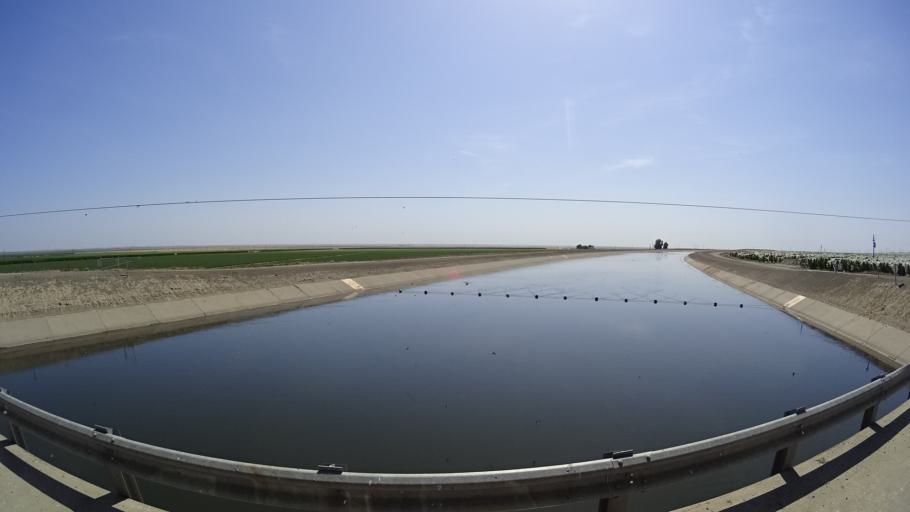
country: US
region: California
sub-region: Kings County
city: Kettleman City
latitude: 36.0478
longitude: -120.0036
